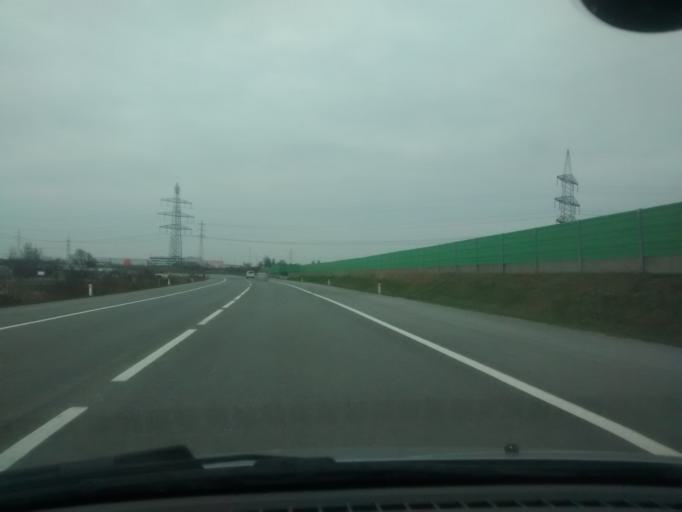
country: AT
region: Lower Austria
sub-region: Politischer Bezirk Wien-Umgebung
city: Leopoldsdorf
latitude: 48.0986
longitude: 16.4061
